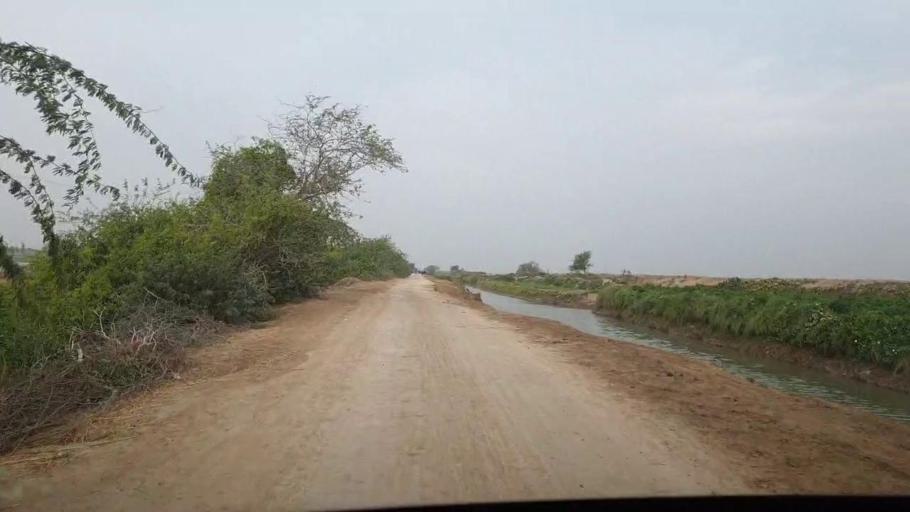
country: PK
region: Sindh
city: Chuhar Jamali
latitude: 24.4002
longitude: 67.9664
